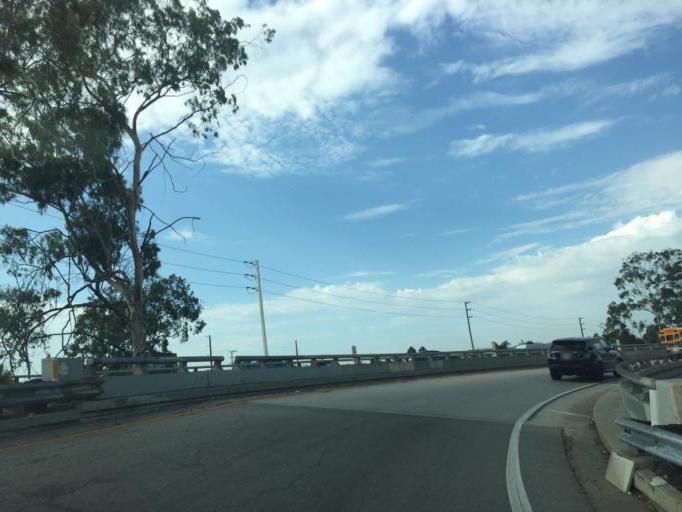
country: US
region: California
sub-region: Los Angeles County
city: Culver City
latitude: 34.0303
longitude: -118.3908
